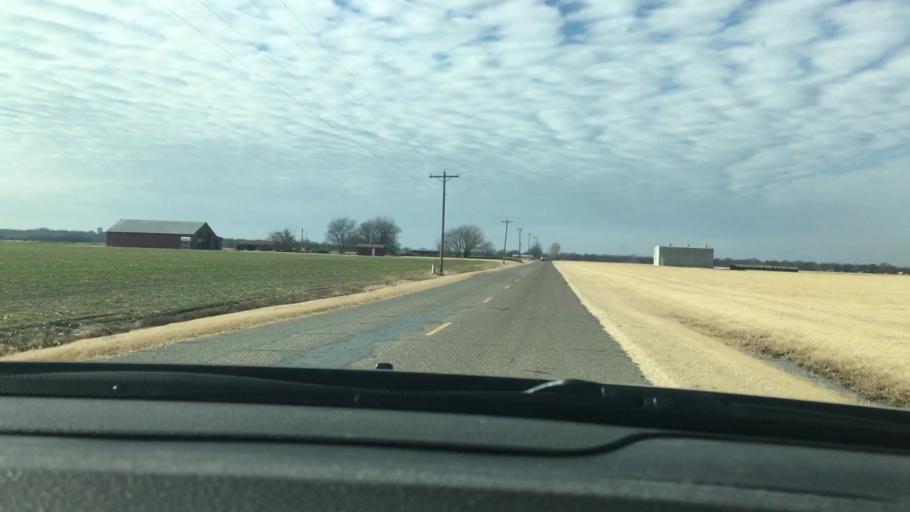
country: US
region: Oklahoma
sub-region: Garvin County
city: Pauls Valley
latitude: 34.7387
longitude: -97.1835
